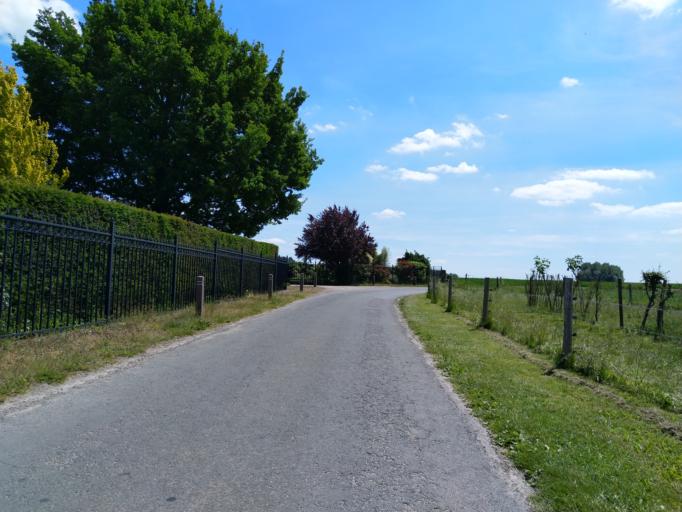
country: BE
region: Wallonia
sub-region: Province du Hainaut
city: Roeulx
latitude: 50.5080
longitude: 4.0433
